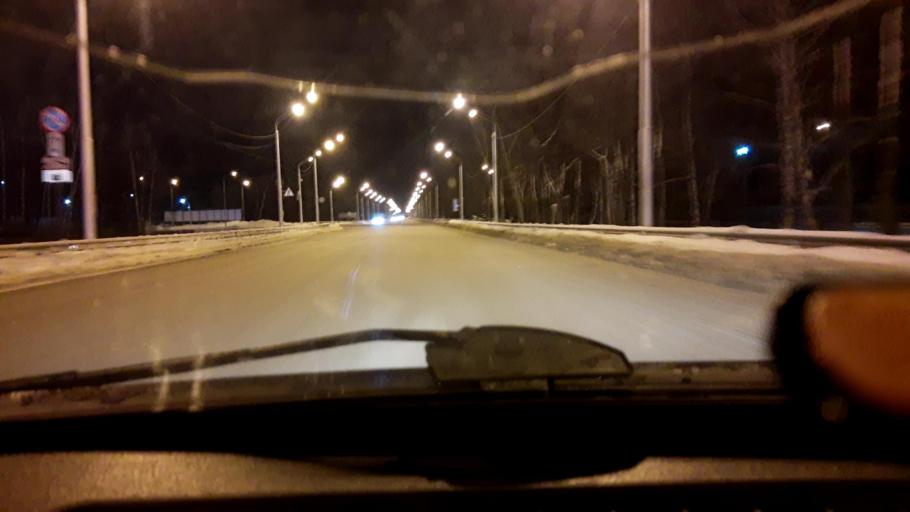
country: RU
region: Bashkortostan
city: Ufa
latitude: 54.5657
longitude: 55.8898
